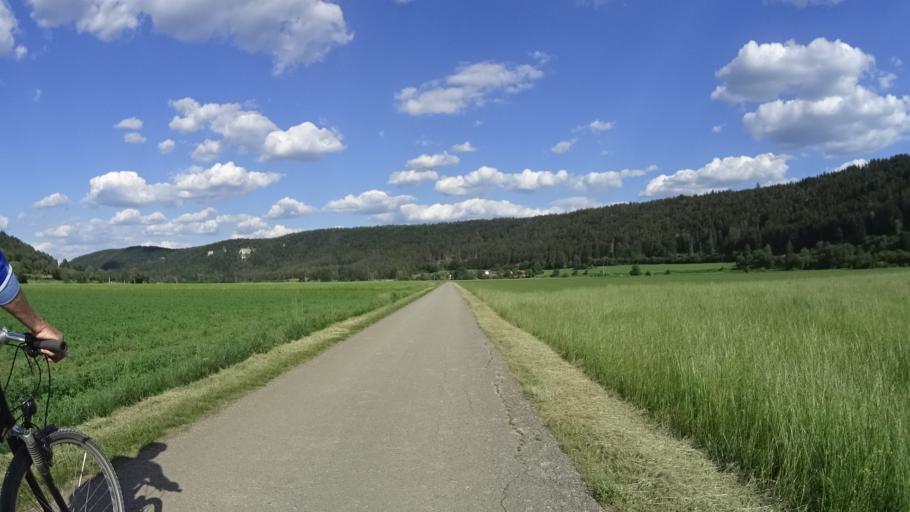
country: DE
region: Bavaria
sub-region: Upper Palatinate
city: Dietfurt
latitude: 49.0125
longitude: 11.5370
